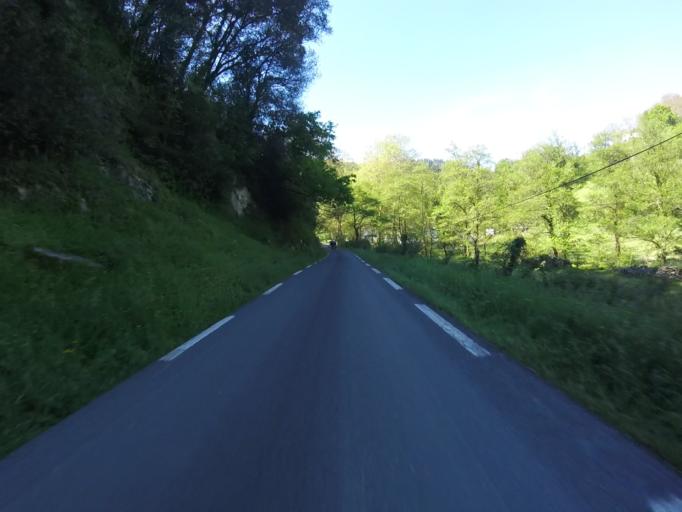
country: ES
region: Basque Country
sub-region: Provincia de Guipuzcoa
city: Errezil
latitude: 43.1761
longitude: -2.2045
